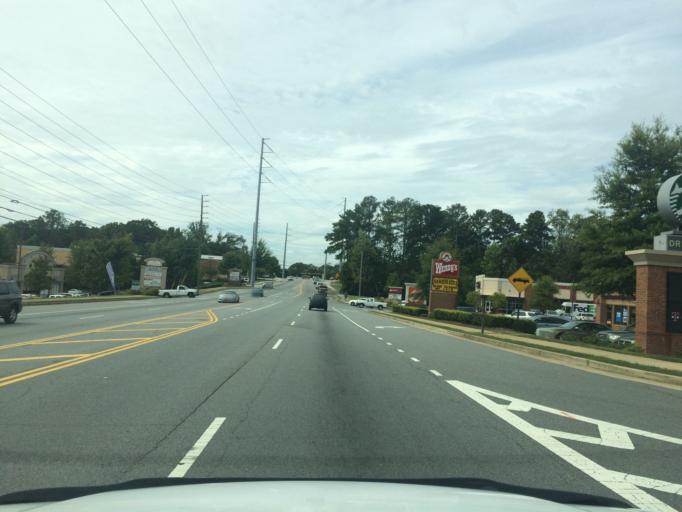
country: US
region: Georgia
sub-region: Cobb County
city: Kennesaw
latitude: 34.0500
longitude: -84.5968
